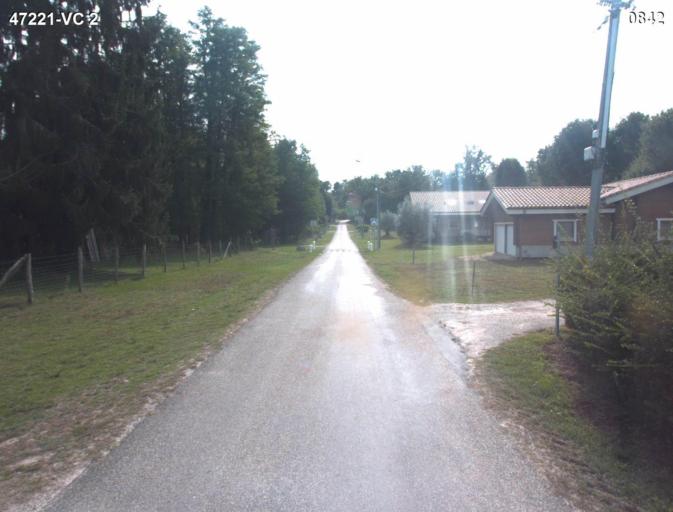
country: FR
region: Aquitaine
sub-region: Departement du Lot-et-Garonne
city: Mezin
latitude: 44.1063
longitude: 0.2317
